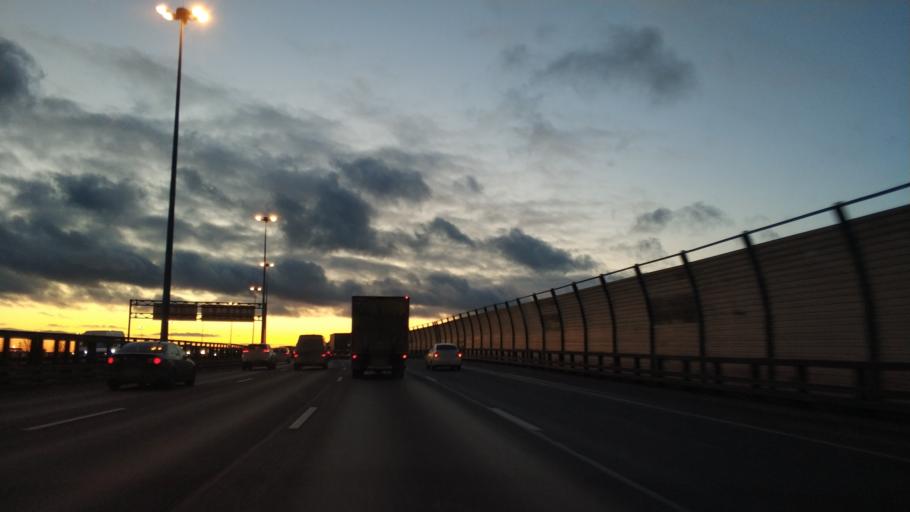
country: RU
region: St.-Petersburg
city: Obukhovo
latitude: 59.8497
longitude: 30.4643
